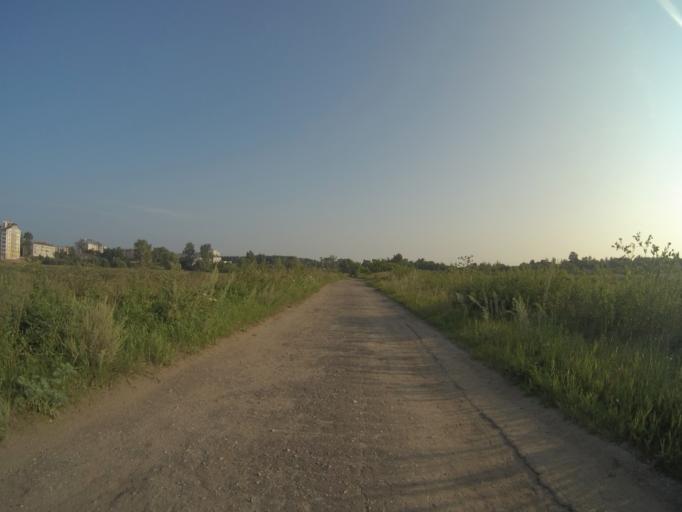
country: RU
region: Vladimir
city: Kommunar
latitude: 56.1148
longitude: 40.4292
